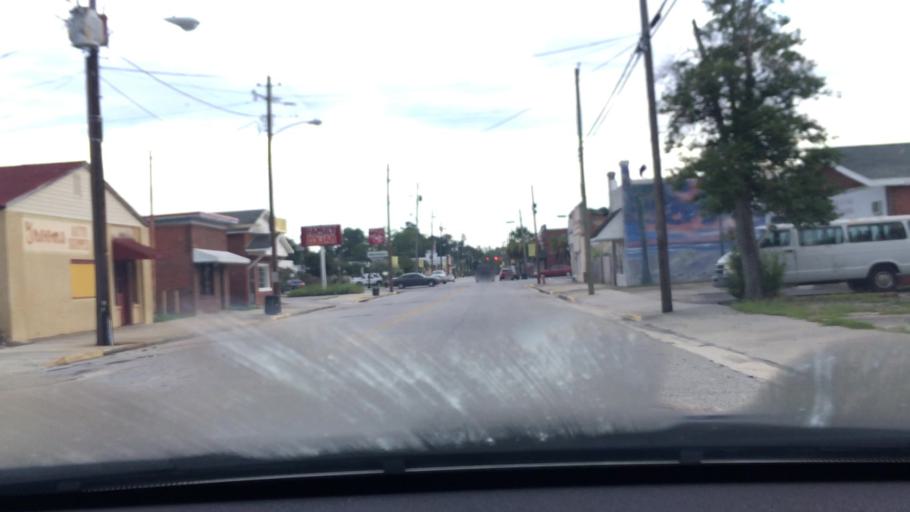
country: US
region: South Carolina
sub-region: Florence County
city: Timmonsville
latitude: 34.1710
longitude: -80.0649
